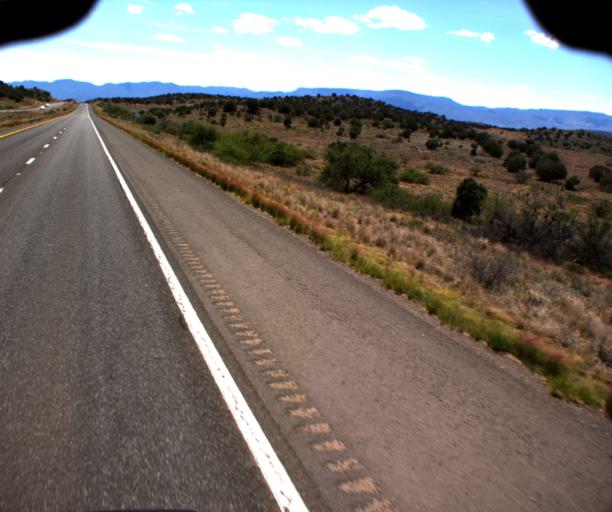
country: US
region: Arizona
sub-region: Yavapai County
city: Cornville
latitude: 34.8129
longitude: -111.9058
